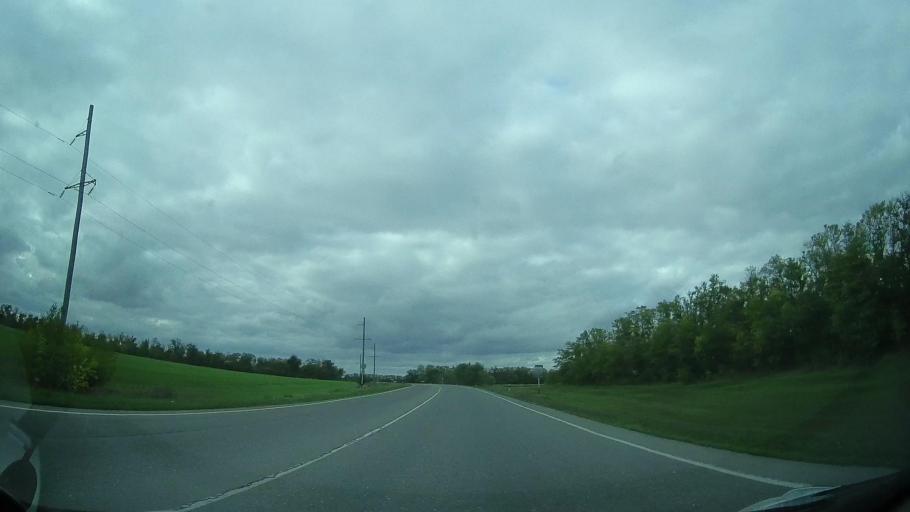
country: RU
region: Rostov
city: Mechetinskaya
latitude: 46.7864
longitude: 40.4083
